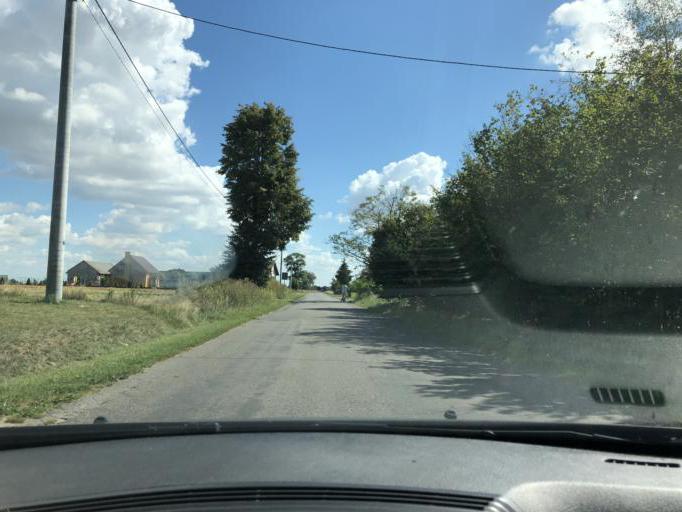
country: PL
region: Lodz Voivodeship
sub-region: Powiat wieruszowski
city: Walichnowy
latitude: 51.2610
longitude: 18.3657
